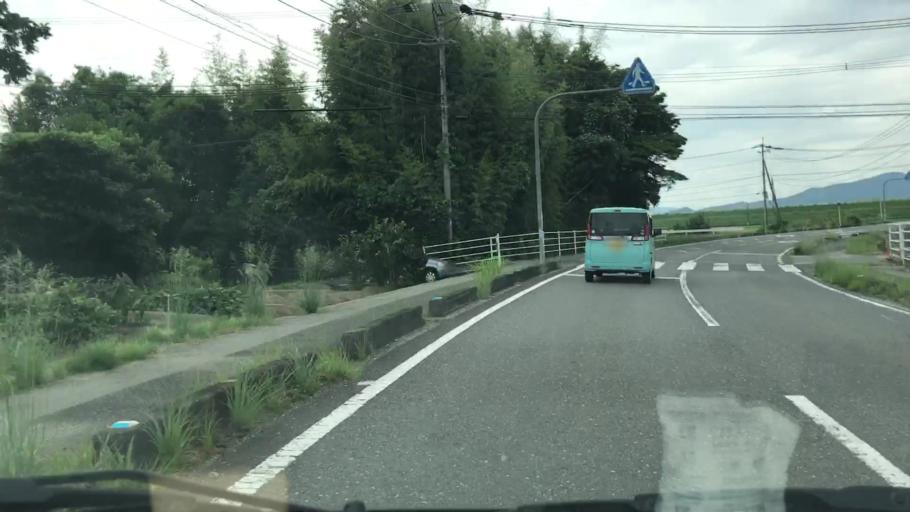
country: JP
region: Saga Prefecture
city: Saga-shi
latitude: 33.2755
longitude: 130.2573
